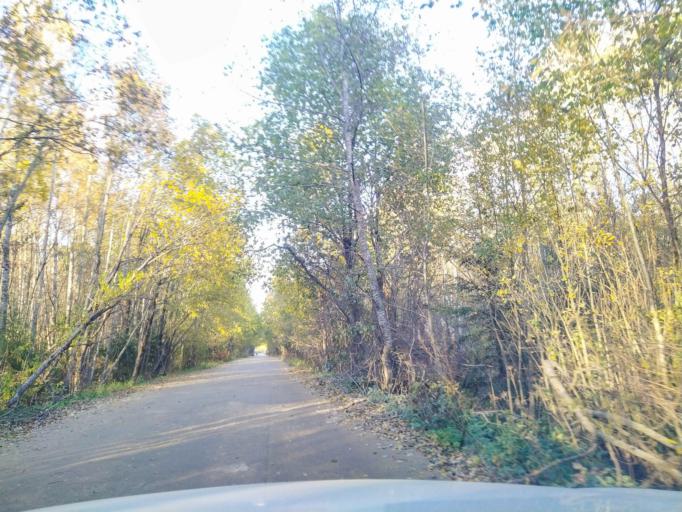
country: RU
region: Leningrad
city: Siverskiy
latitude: 59.2965
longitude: 30.0341
